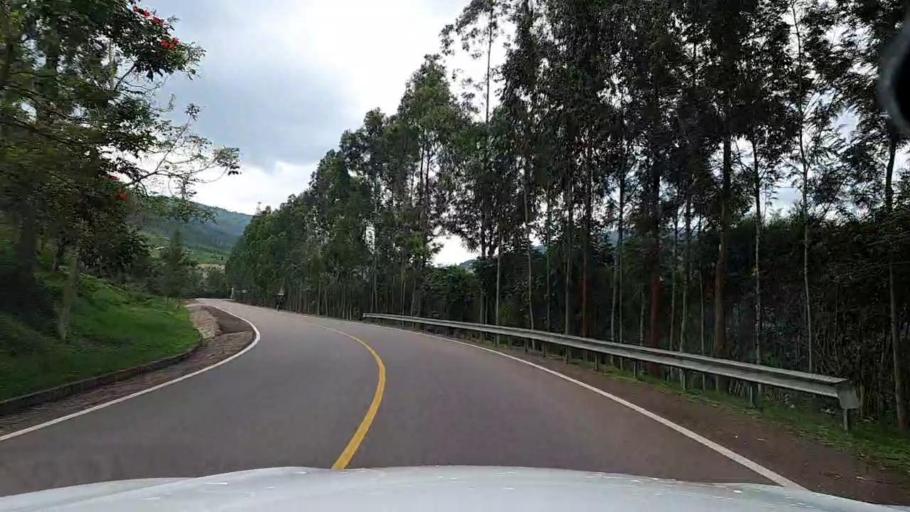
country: RW
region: Northern Province
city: Byumba
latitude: -1.6817
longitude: 30.1039
